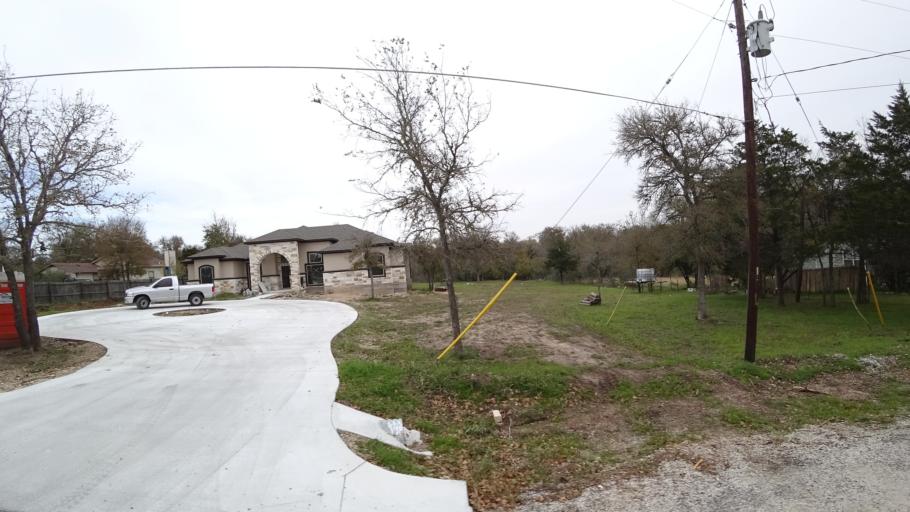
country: US
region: Texas
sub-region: Travis County
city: Garfield
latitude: 30.1006
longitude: -97.5673
